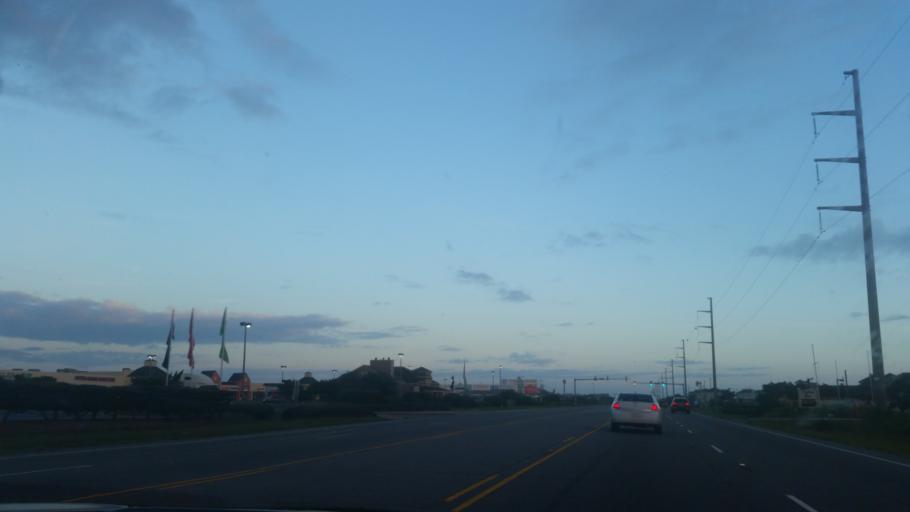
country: US
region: North Carolina
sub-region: Dare County
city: Nags Head
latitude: 35.9362
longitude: -75.6143
